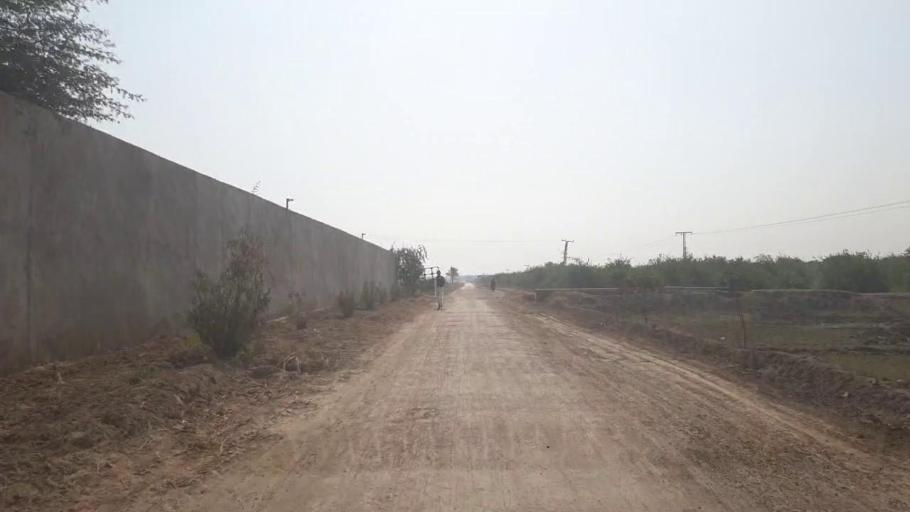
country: PK
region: Sindh
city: Tando Allahyar
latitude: 25.4654
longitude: 68.8126
